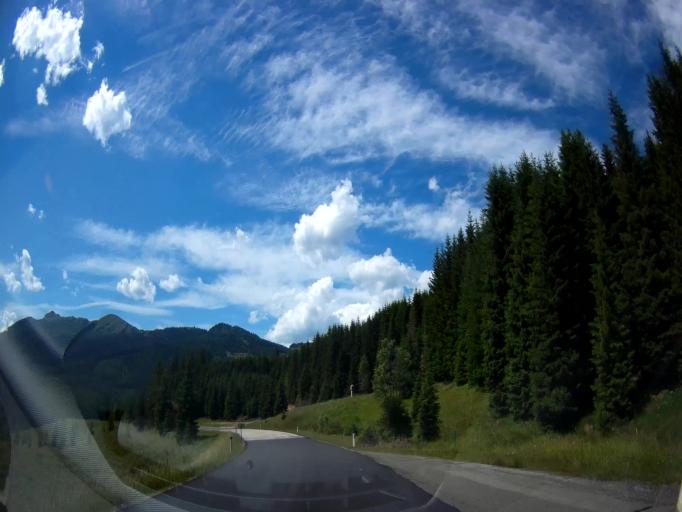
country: AT
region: Styria
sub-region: Politischer Bezirk Murau
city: Stadl an der Mur
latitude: 46.9710
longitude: 14.0160
